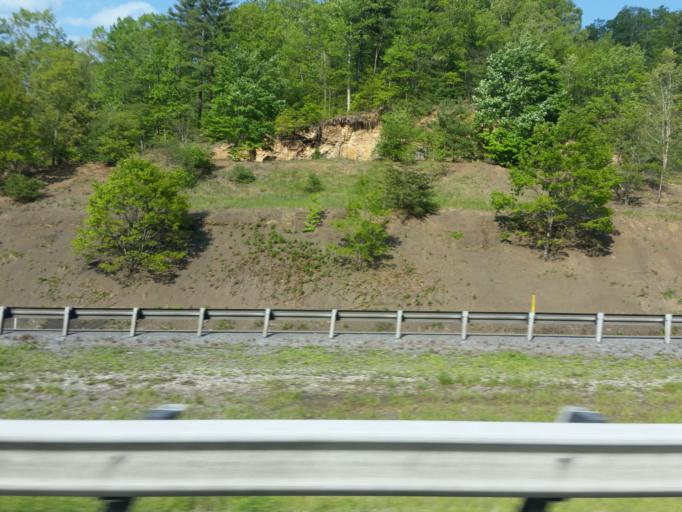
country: US
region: West Virginia
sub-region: Mercer County
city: Athens
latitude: 37.4438
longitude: -81.0663
